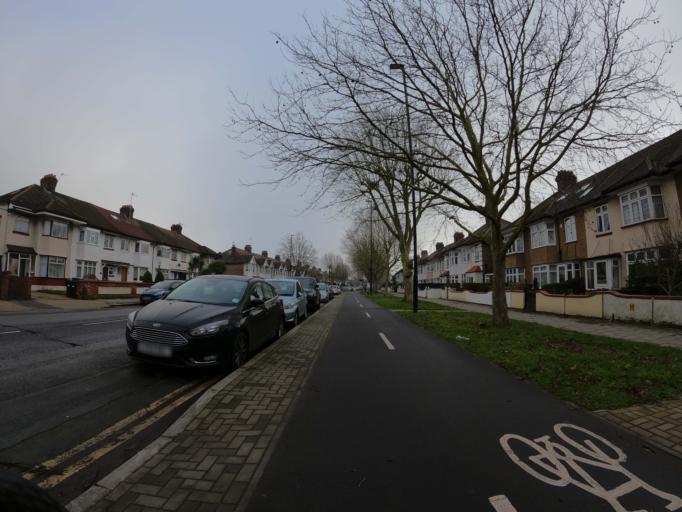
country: GB
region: England
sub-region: Greater London
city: Brentford
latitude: 51.4950
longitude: -0.3225
